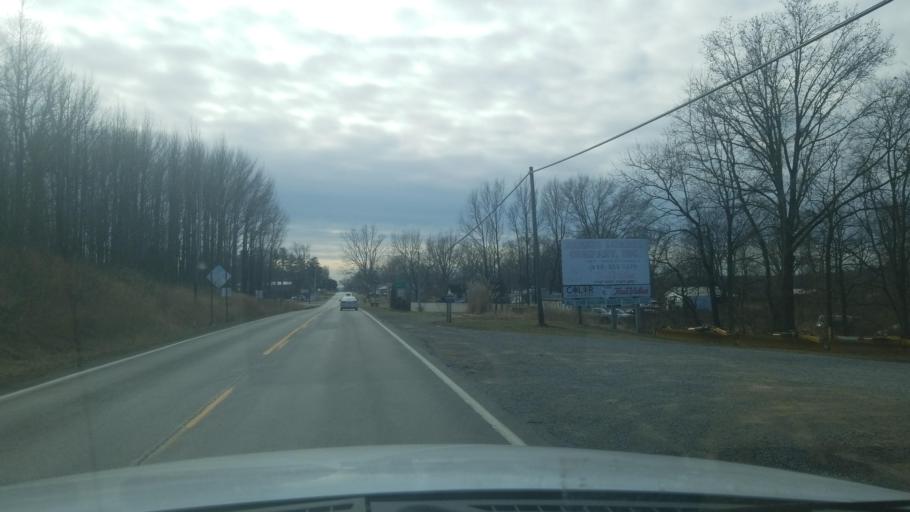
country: US
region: Illinois
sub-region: Saline County
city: Harrisburg
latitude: 37.7171
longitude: -88.5359
